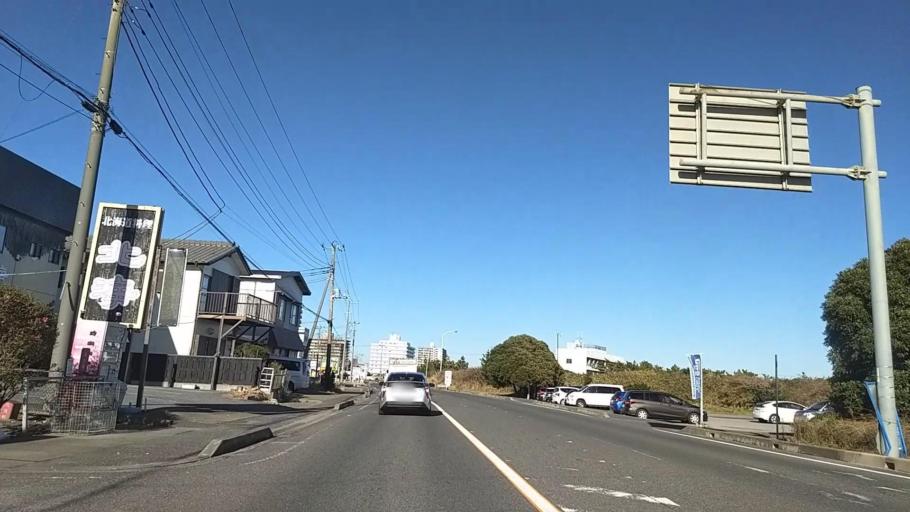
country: JP
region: Chiba
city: Mobara
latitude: 35.4455
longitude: 140.4010
